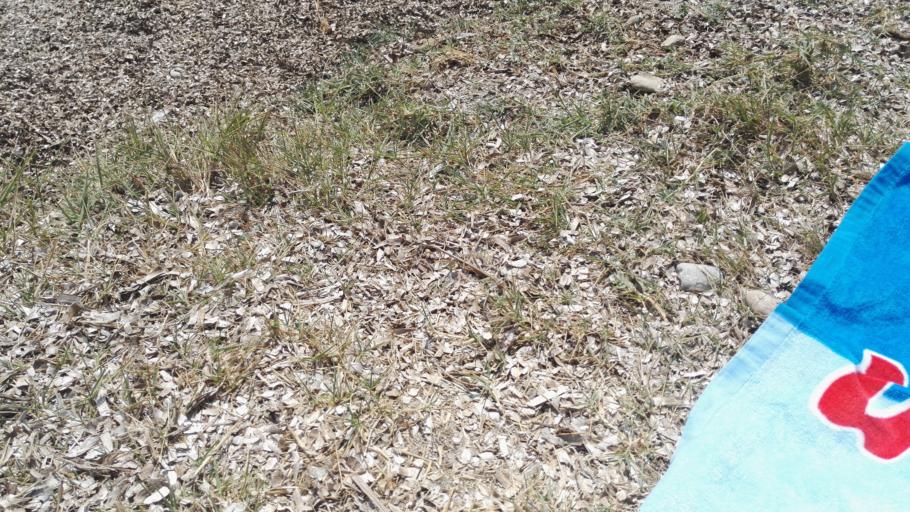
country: IT
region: Apulia
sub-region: Provincia di Lecce
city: Borgagne
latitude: 40.2545
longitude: 18.4448
